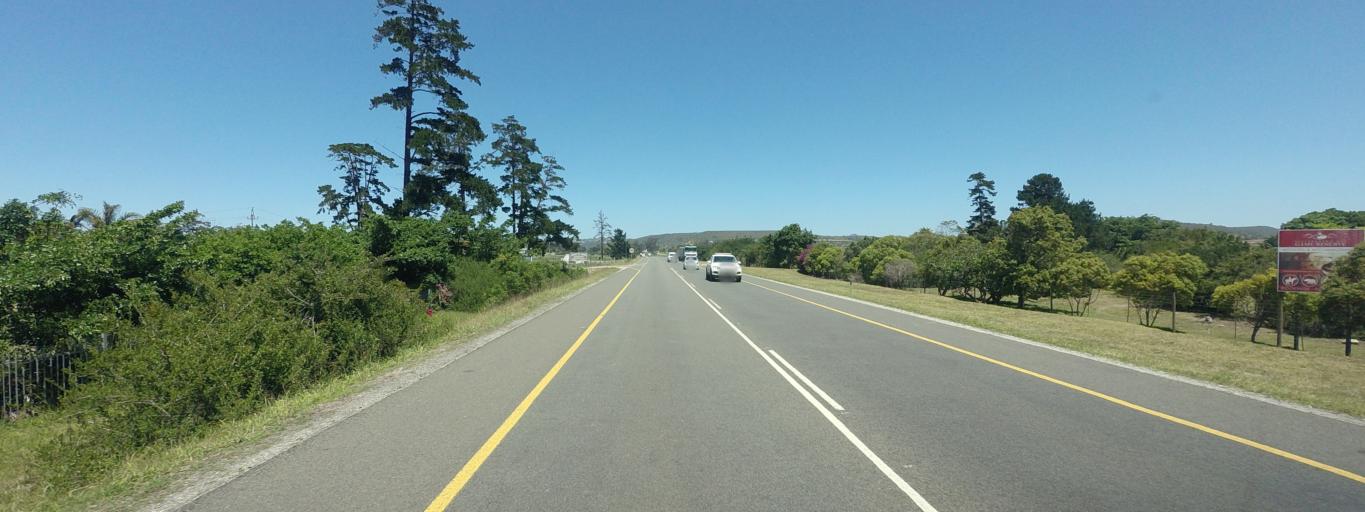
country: ZA
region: Western Cape
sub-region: Eden District Municipality
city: Plettenberg Bay
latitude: -34.0110
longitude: 23.3902
